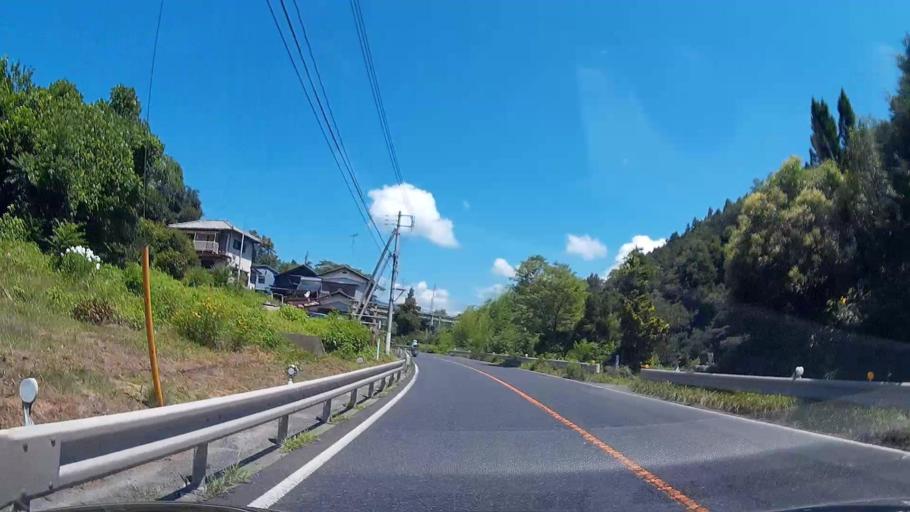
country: JP
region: Gunma
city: Numata
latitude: 36.6290
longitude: 139.0388
